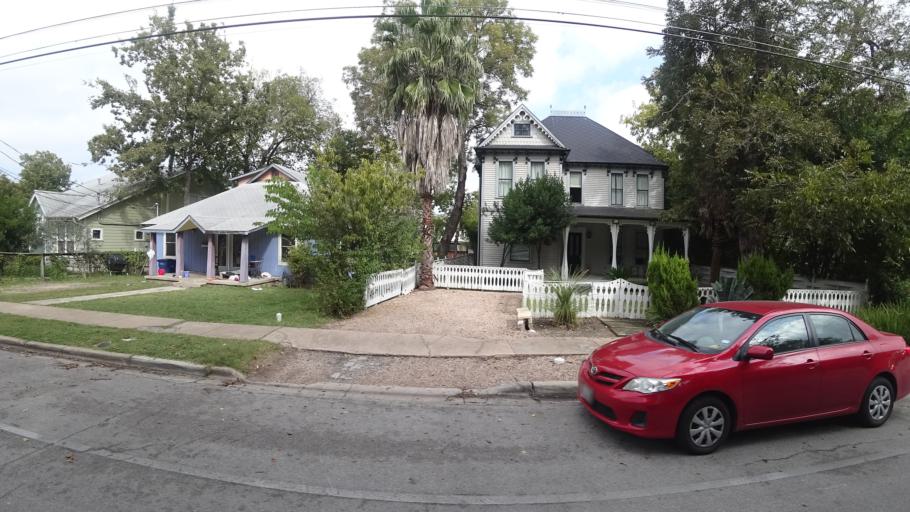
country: US
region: Texas
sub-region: Travis County
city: Austin
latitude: 30.2468
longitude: -97.7573
